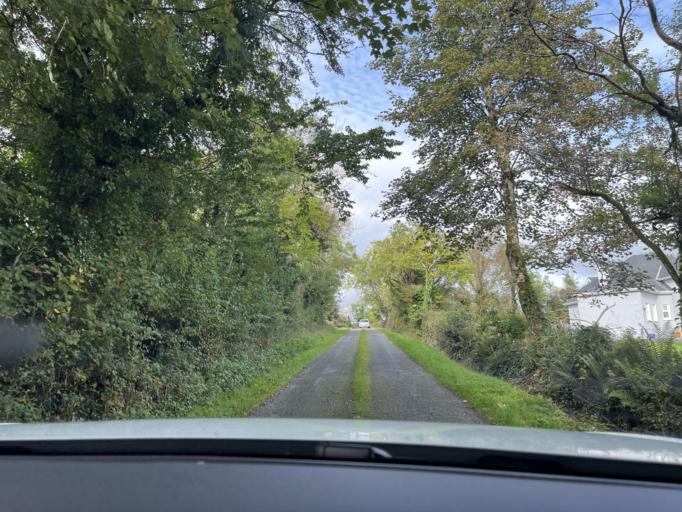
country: IE
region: Connaught
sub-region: County Leitrim
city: Carrick-on-Shannon
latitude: 53.9678
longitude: -8.0752
